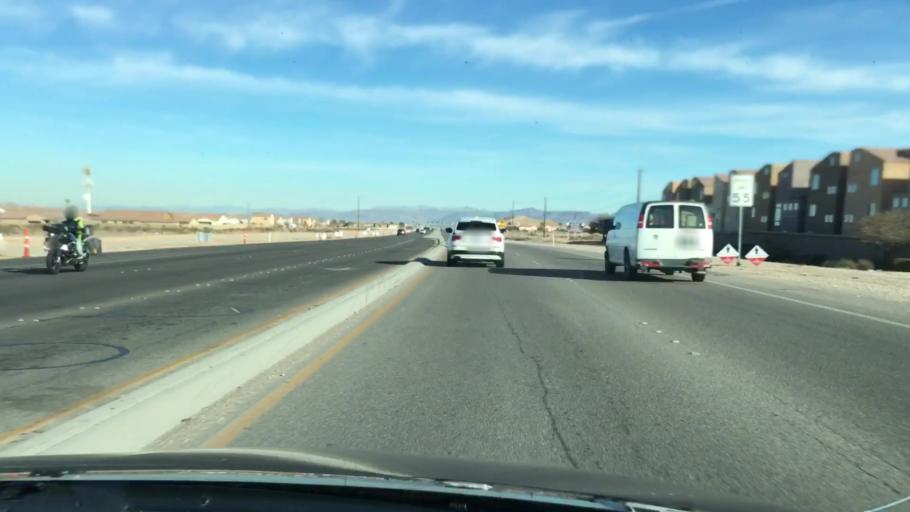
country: US
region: Nevada
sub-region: Clark County
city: Enterprise
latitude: 36.0204
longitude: -115.2973
